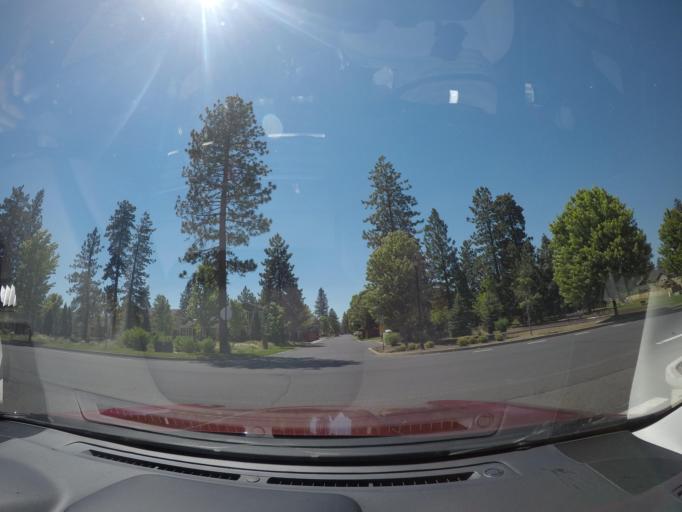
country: US
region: Oregon
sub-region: Deschutes County
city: Sisters
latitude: 44.2962
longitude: -121.5667
